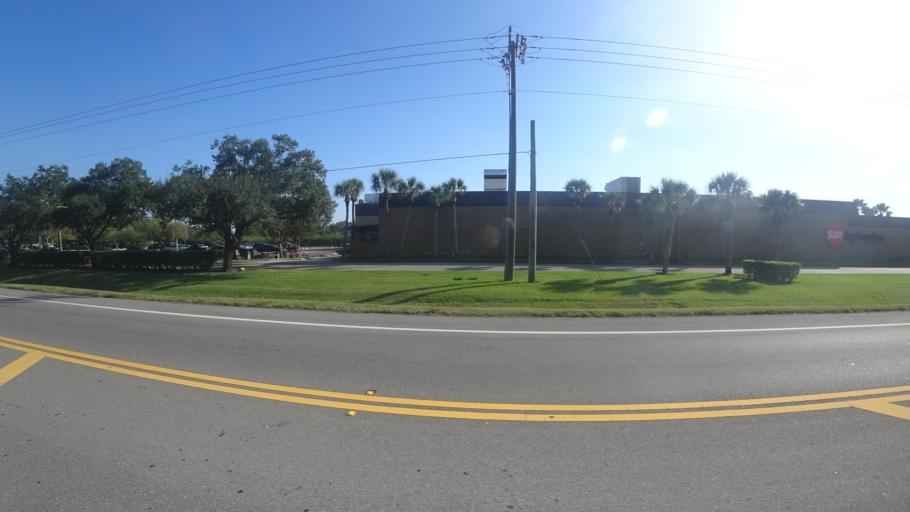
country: US
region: Florida
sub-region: Sarasota County
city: North Sarasota
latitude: 27.3890
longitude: -82.5391
